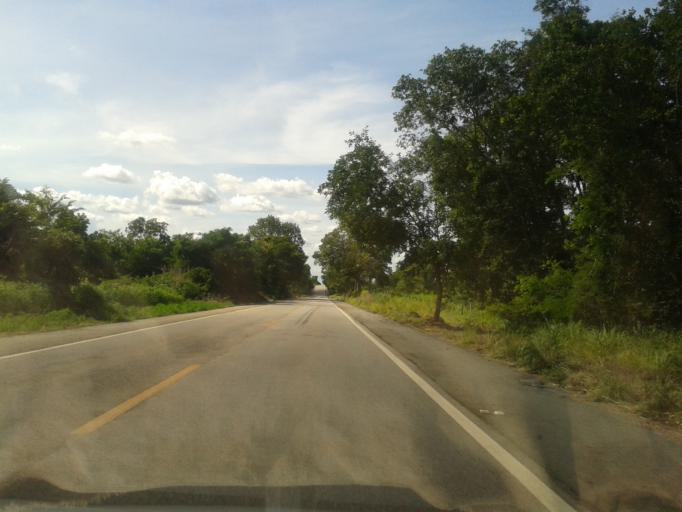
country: BR
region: Goias
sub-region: Mozarlandia
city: Mozarlandia
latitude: -15.2375
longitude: -50.5141
